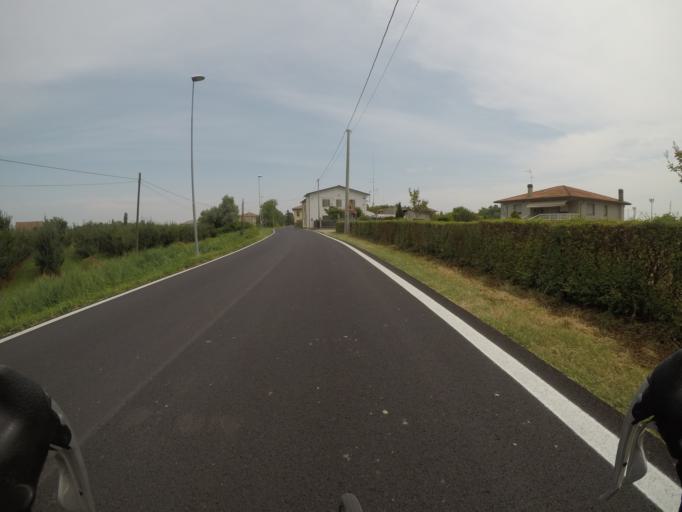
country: IT
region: Veneto
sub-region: Provincia di Rovigo
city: Costa di Rovigo
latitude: 45.0465
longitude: 11.6851
